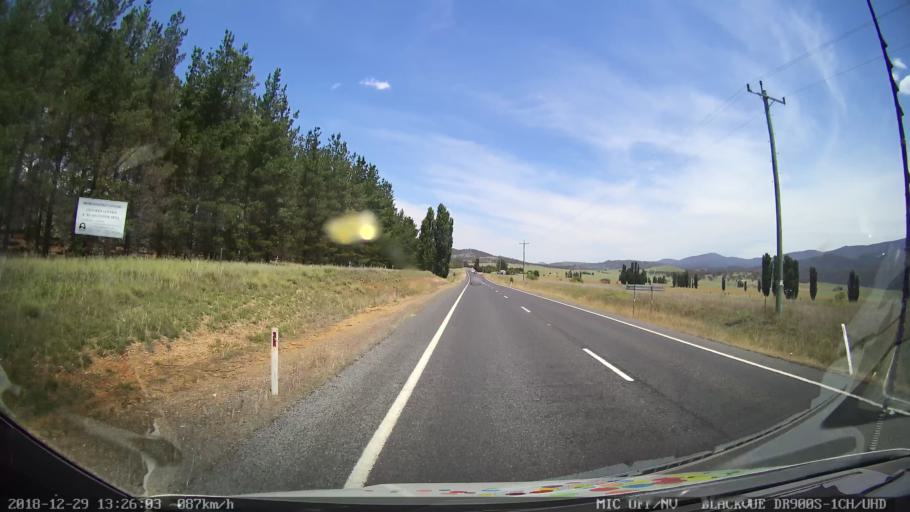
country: AU
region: New South Wales
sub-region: Cooma-Monaro
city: Cooma
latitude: -35.8504
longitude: 149.1600
